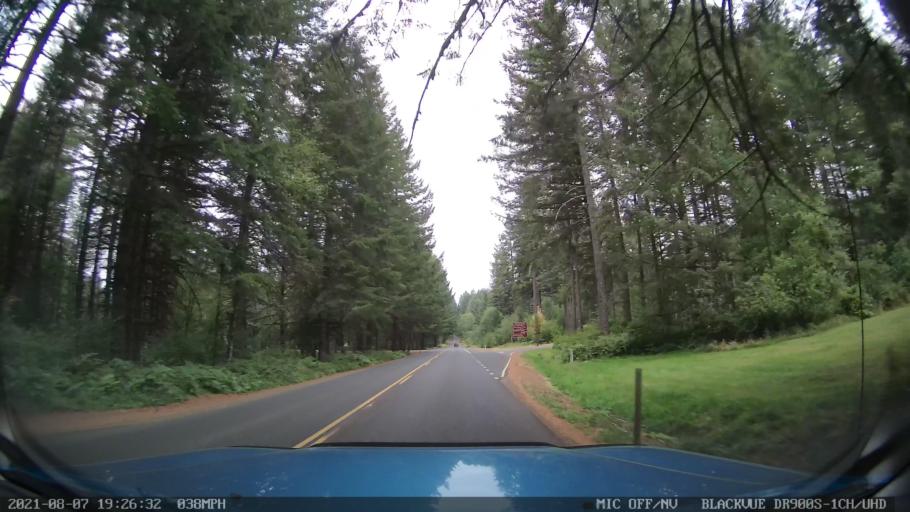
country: US
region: Oregon
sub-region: Linn County
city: Lyons
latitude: 44.8729
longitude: -122.6517
